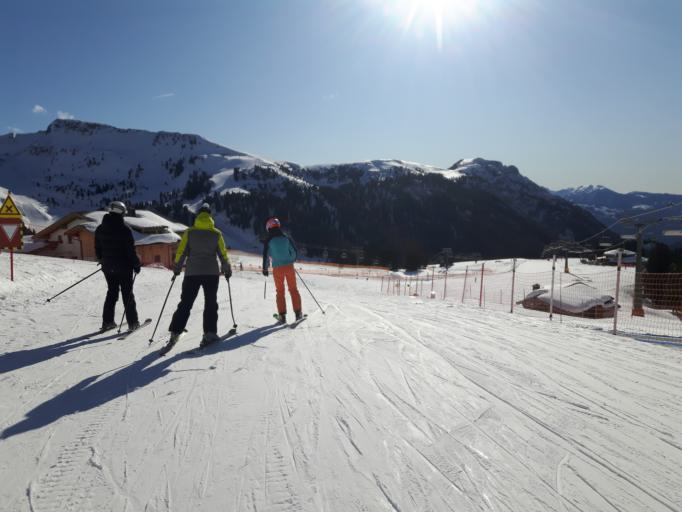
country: IT
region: Trentino-Alto Adige
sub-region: Provincia di Trento
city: Panchia
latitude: 46.3505
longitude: 11.5477
